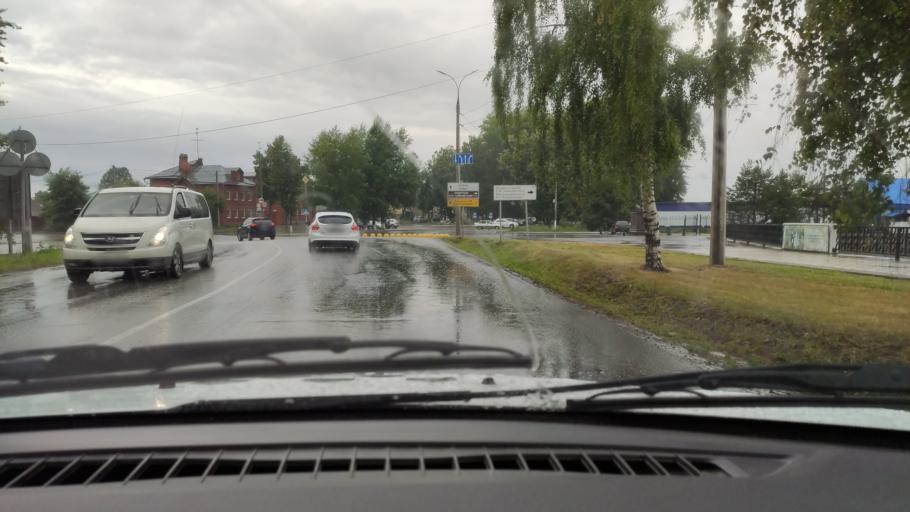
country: RU
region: Udmurtiya
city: Votkinsk
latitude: 57.0517
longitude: 53.9737
